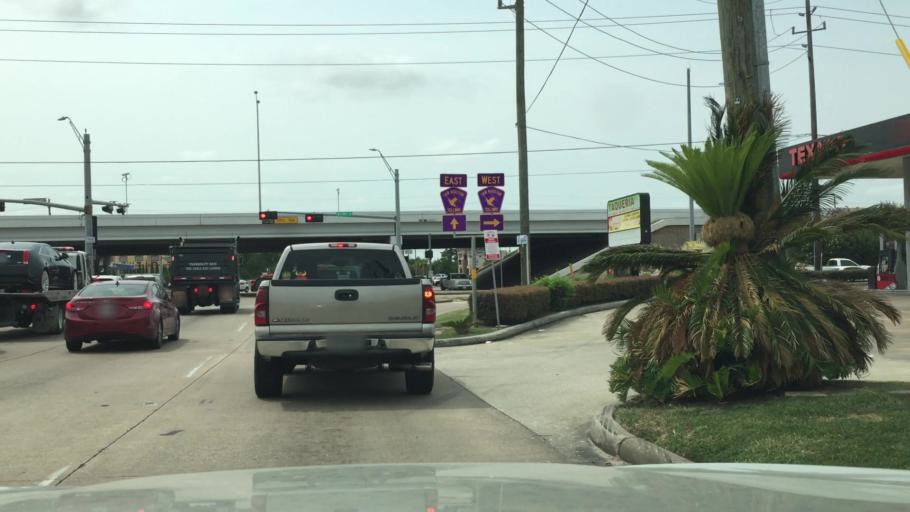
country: US
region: Texas
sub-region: Harris County
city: Jersey Village
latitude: 29.9307
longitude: -95.5448
